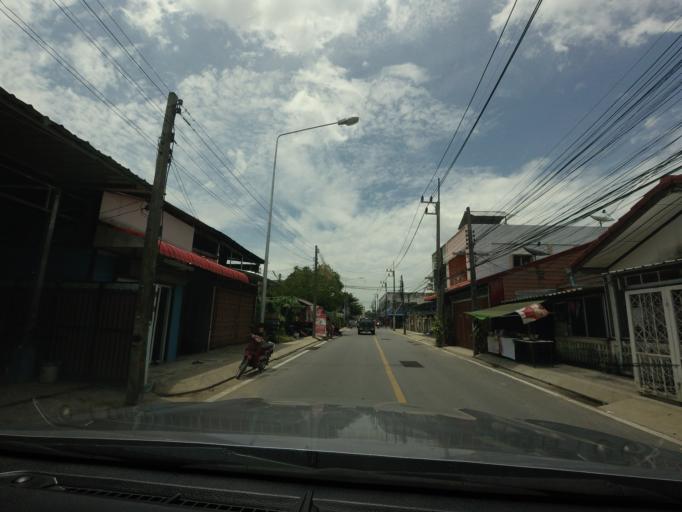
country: TH
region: Yala
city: Yala
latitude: 6.5373
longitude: 101.2897
